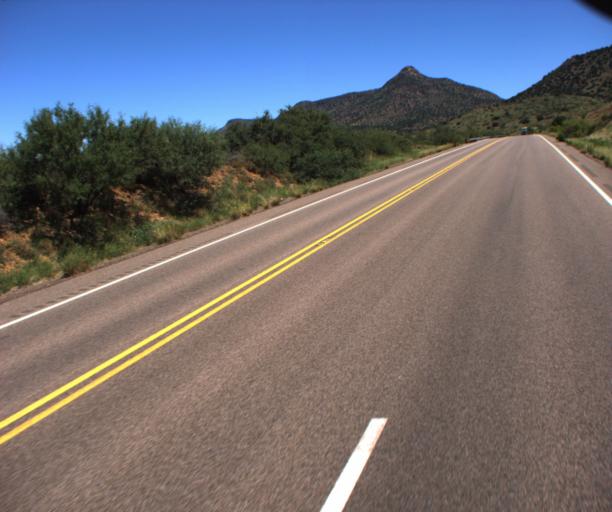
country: US
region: Arizona
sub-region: Gila County
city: Globe
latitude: 33.5974
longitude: -110.6375
